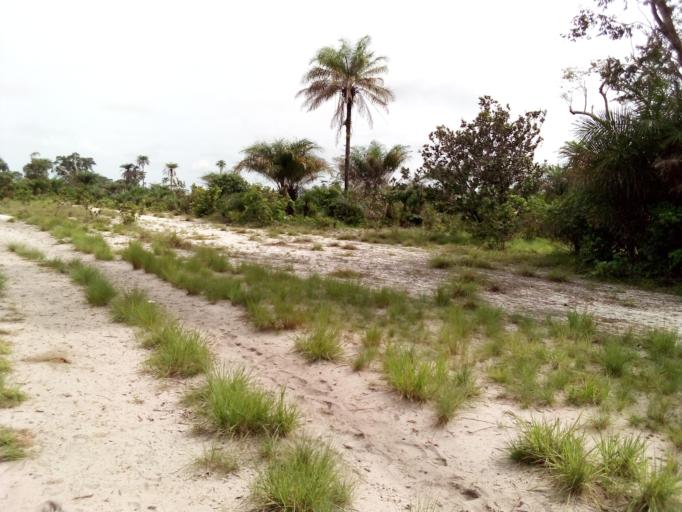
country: SL
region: Southern Province
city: Bonthe
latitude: 7.5163
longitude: -12.5695
